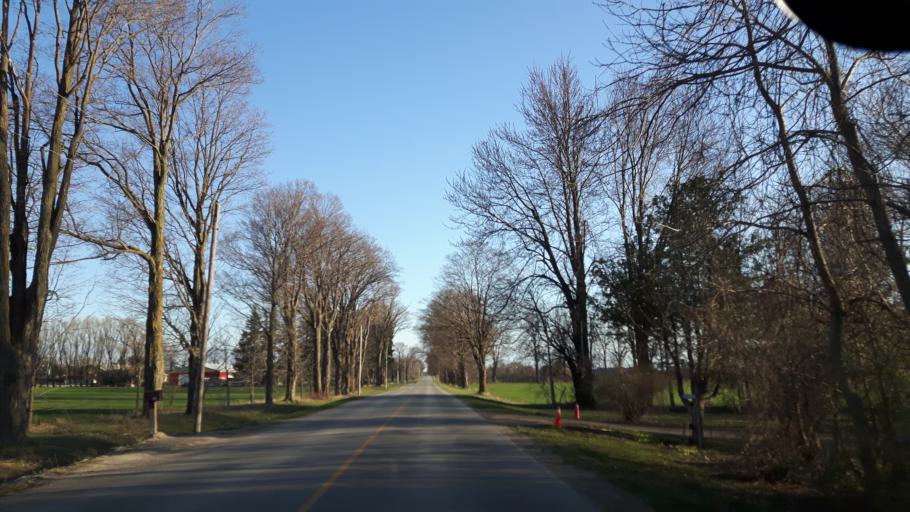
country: CA
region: Ontario
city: Goderich
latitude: 43.7063
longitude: -81.6850
